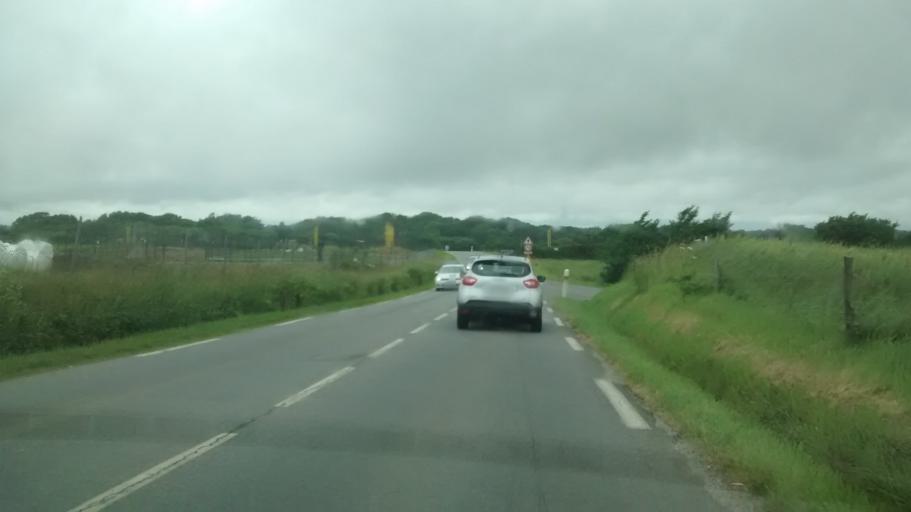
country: FR
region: Brittany
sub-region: Departement du Morbihan
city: Queven
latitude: 47.7624
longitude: -3.4244
